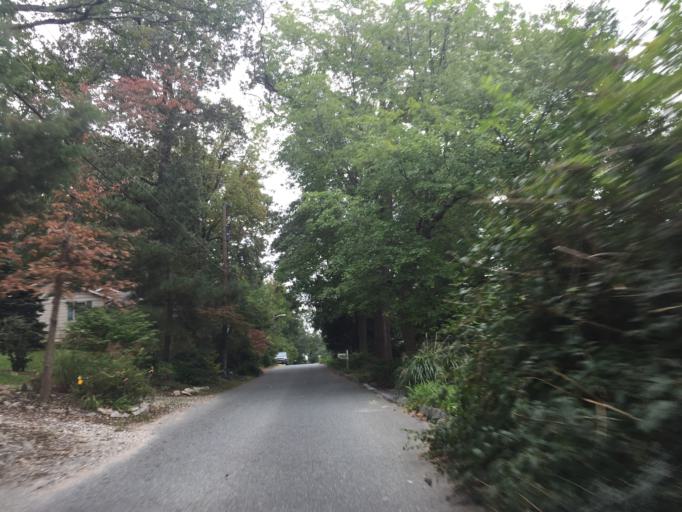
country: US
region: Maryland
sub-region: Baltimore County
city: Middle River
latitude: 39.3515
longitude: -76.4331
